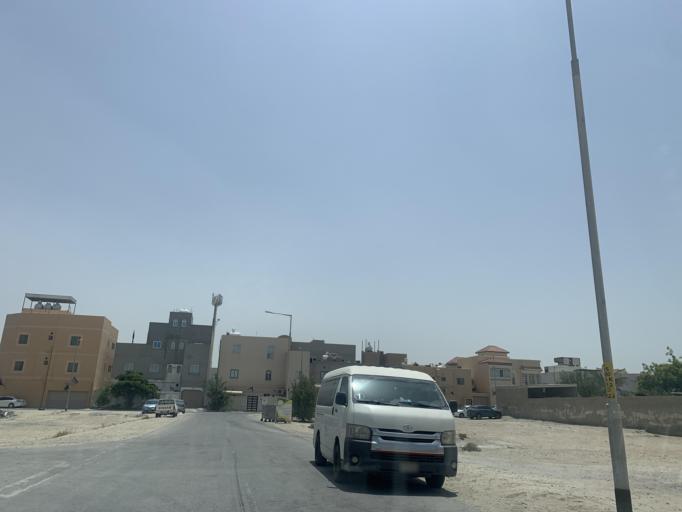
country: BH
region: Central Governorate
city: Madinat Hamad
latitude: 26.1468
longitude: 50.5035
